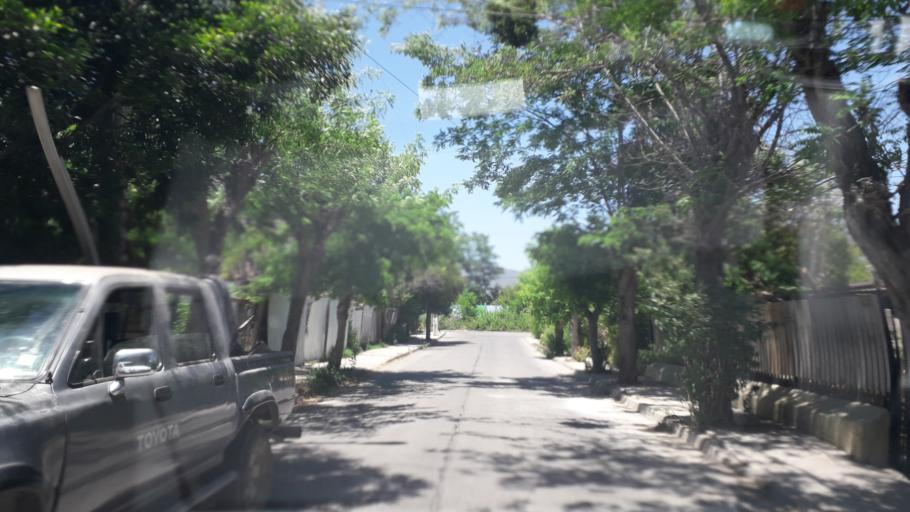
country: CL
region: Valparaiso
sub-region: Provincia de Quillota
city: Quillota
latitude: -32.9367
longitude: -71.2718
